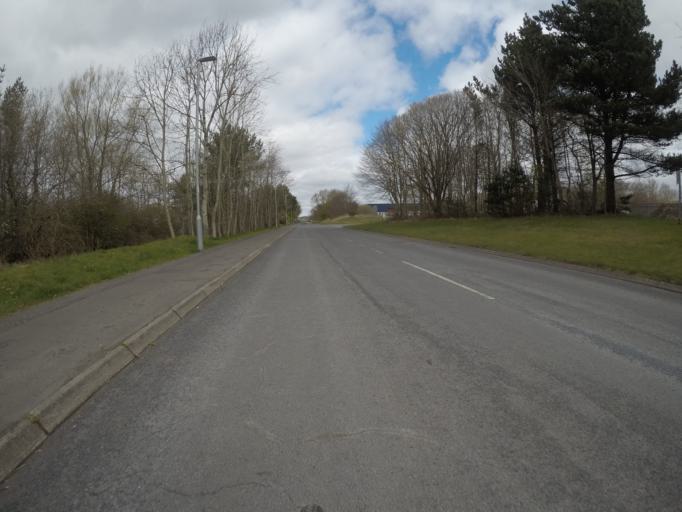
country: GB
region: Scotland
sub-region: North Ayrshire
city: Irvine
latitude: 55.6158
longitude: -4.6449
